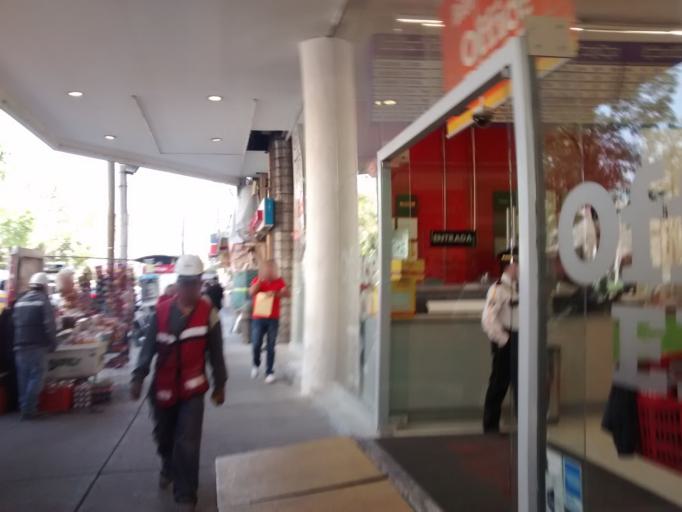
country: MX
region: Mexico City
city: Miguel Hidalgo
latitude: 19.4382
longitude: -99.2017
